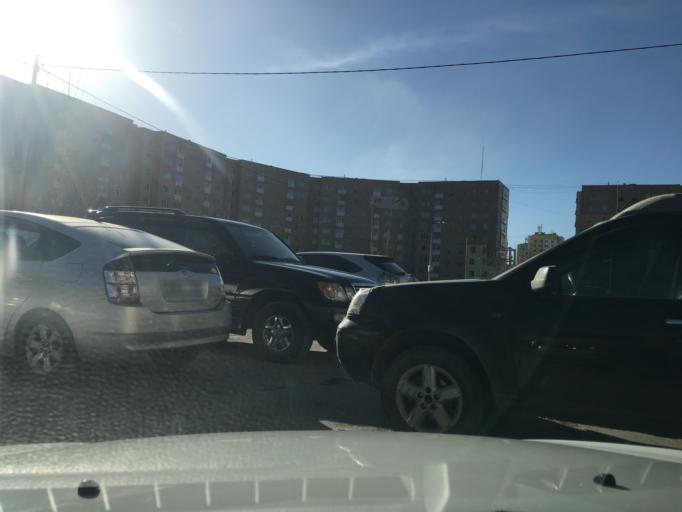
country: MN
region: Ulaanbaatar
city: Ulaanbaatar
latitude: 47.9138
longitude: 106.8487
